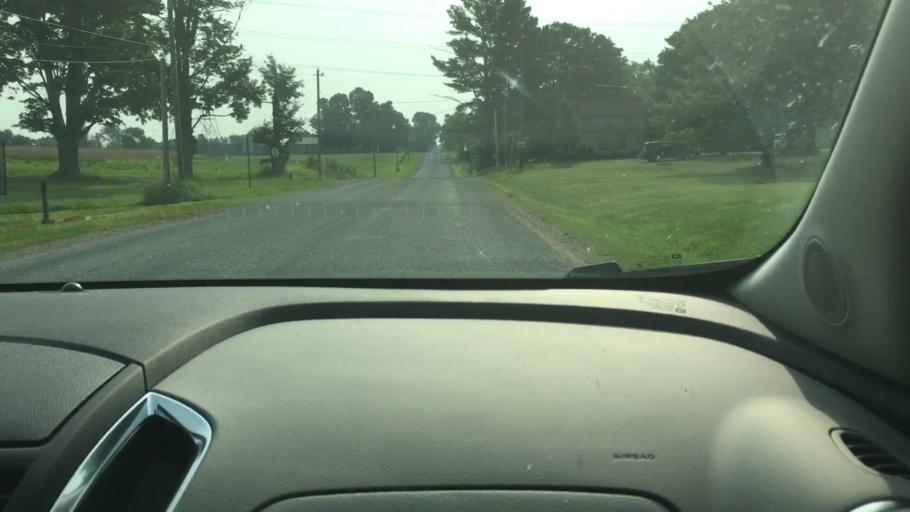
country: US
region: Michigan
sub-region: Cass County
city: Marcellus
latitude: 42.0269
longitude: -85.7968
